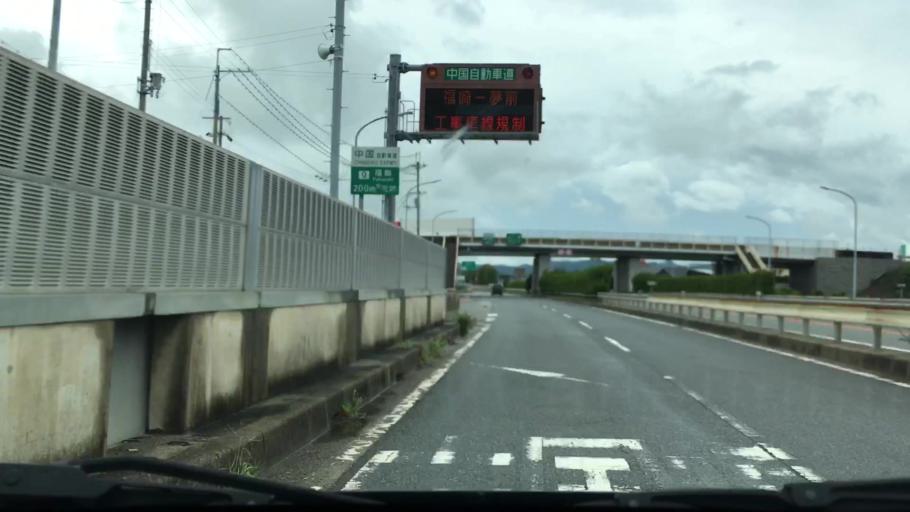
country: JP
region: Hyogo
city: Himeji
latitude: 34.9465
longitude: 134.7636
